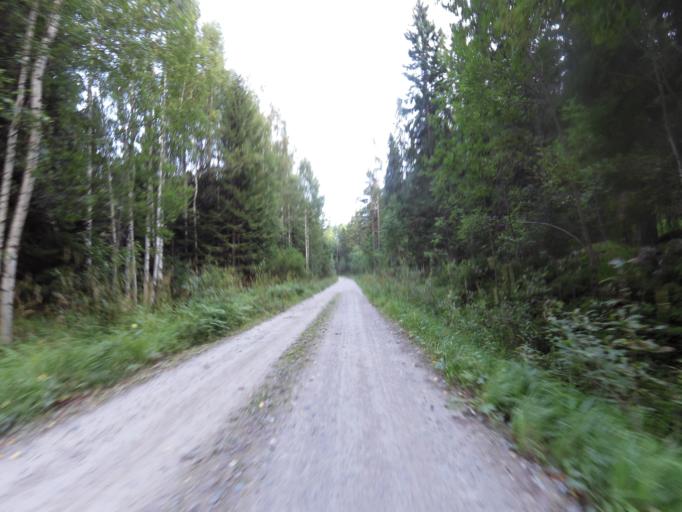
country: SE
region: Gaevleborg
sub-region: Gavle Kommun
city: Gavle
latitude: 60.7072
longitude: 17.1237
